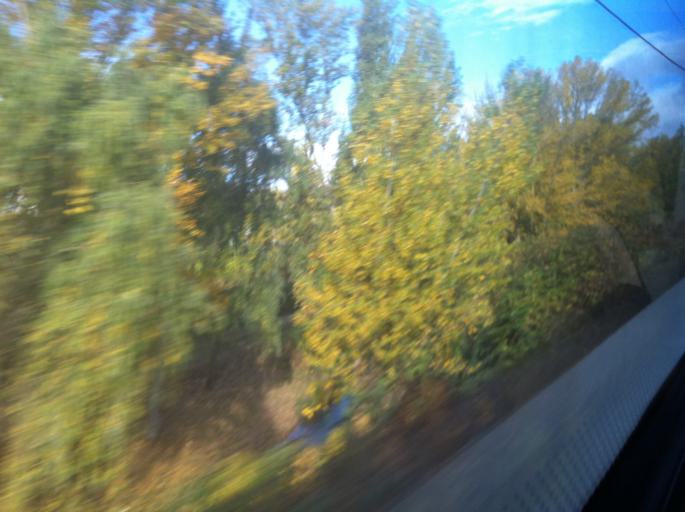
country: ES
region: Castille and Leon
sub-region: Provincia de Burgos
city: Briviesca
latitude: 42.5497
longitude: -3.3189
